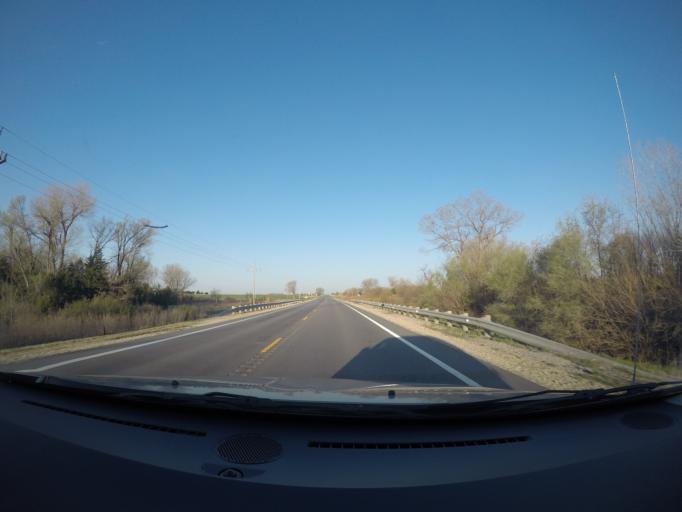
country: US
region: Kansas
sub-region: Stafford County
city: Stafford
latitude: 37.8073
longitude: -98.4389
